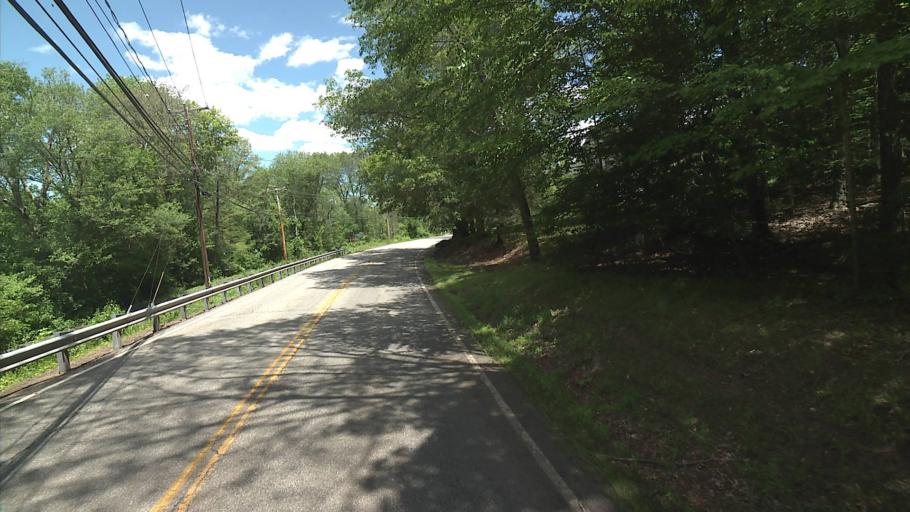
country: US
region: Connecticut
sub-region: Middlesex County
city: East Hampton
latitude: 41.5575
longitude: -72.5111
